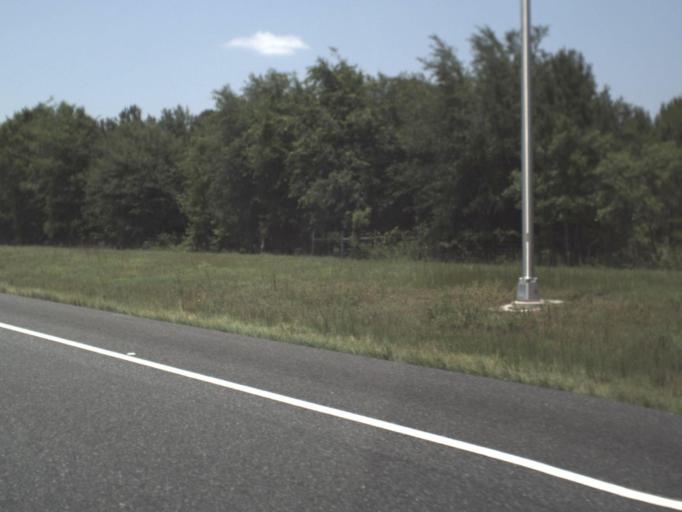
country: US
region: Florida
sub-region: Suwannee County
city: Wellborn
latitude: 30.2660
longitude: -82.7492
